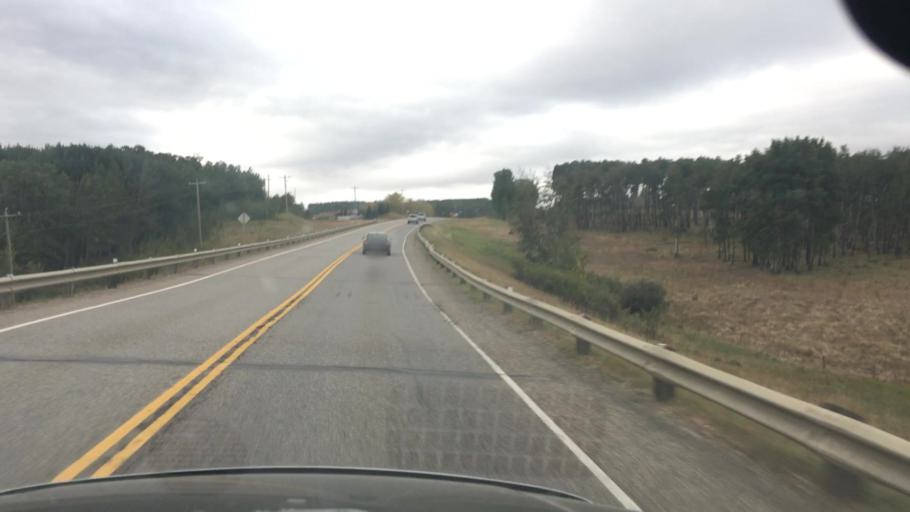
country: CA
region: Alberta
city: Cochrane
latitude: 51.3706
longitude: -114.4702
